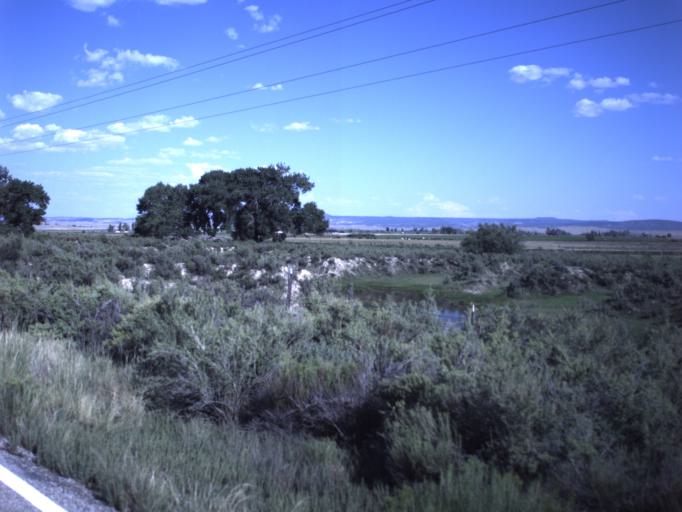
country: US
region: Utah
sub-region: Emery County
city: Huntington
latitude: 39.3458
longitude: -110.8868
